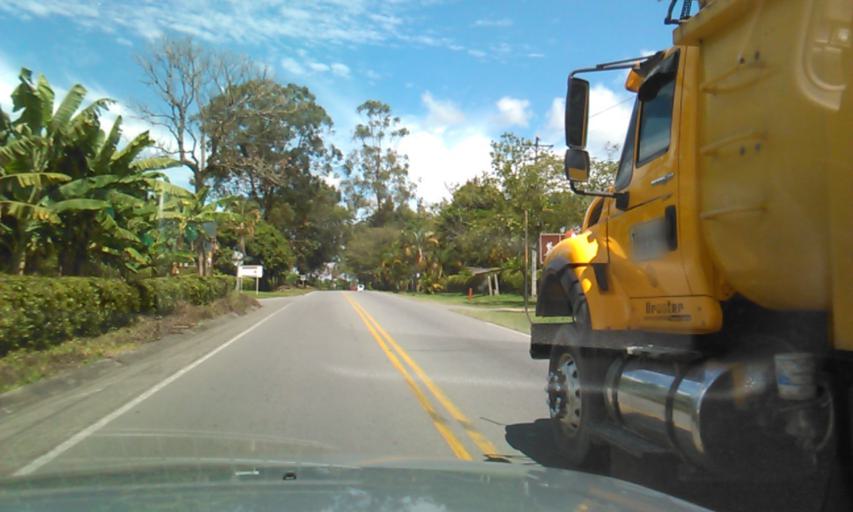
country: CO
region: Quindio
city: Cordoba
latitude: 4.4443
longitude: -75.7178
